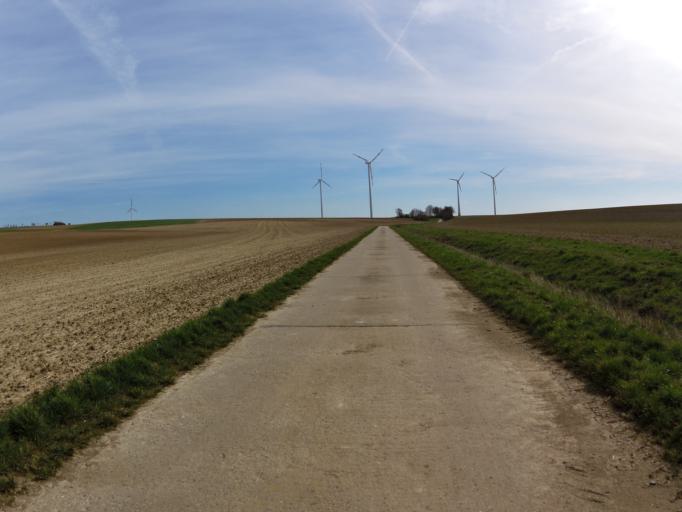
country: DE
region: Bavaria
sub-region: Regierungsbezirk Unterfranken
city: Biebelried
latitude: 49.7612
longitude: 10.0866
